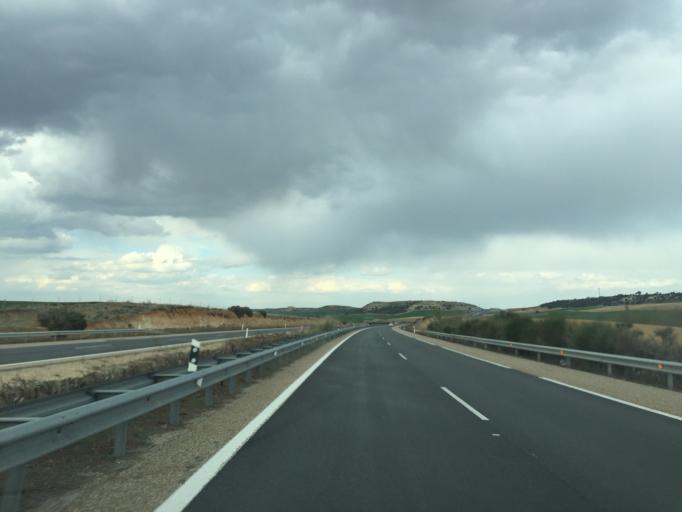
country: ES
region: Castille and Leon
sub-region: Provincia de Zamora
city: Canizal
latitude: 41.1866
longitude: -5.3602
